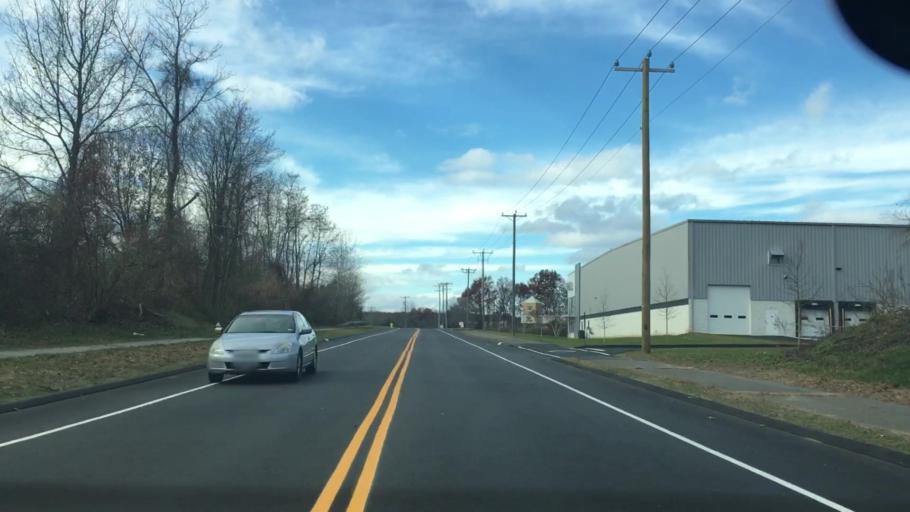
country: US
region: Connecticut
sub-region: Hartford County
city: Plainville
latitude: 41.6935
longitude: -72.8570
